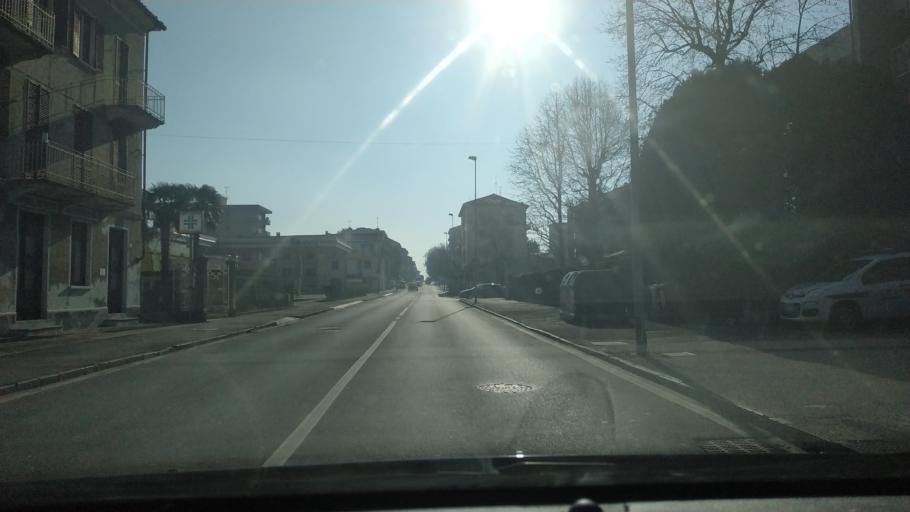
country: IT
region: Piedmont
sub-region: Provincia di Torino
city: Ivrea
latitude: 45.4553
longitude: 7.8791
